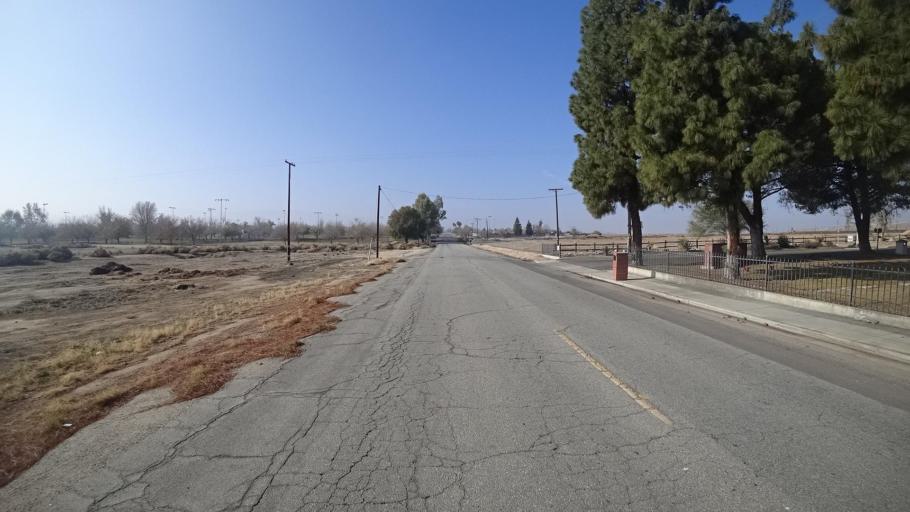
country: US
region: California
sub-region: Kern County
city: Ford City
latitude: 35.1546
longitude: -119.4376
